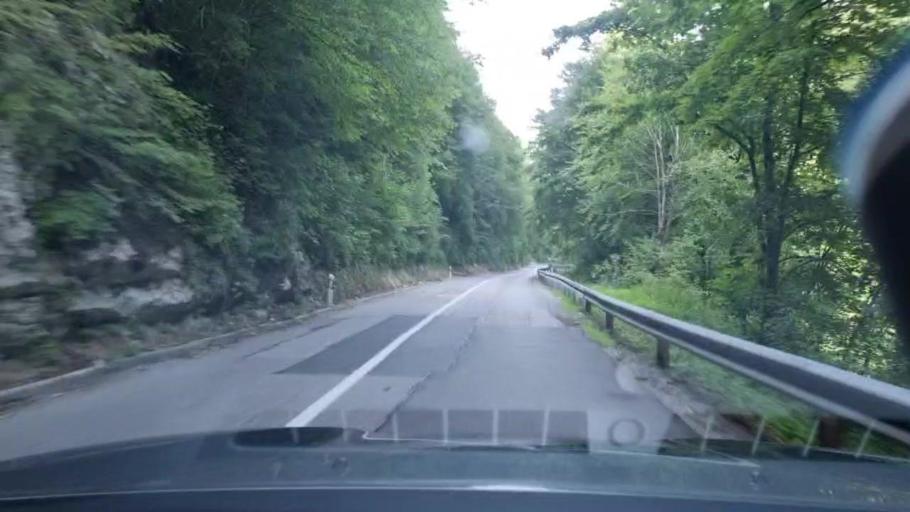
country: BA
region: Federation of Bosnia and Herzegovina
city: Stijena
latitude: 44.8773
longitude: 16.0722
